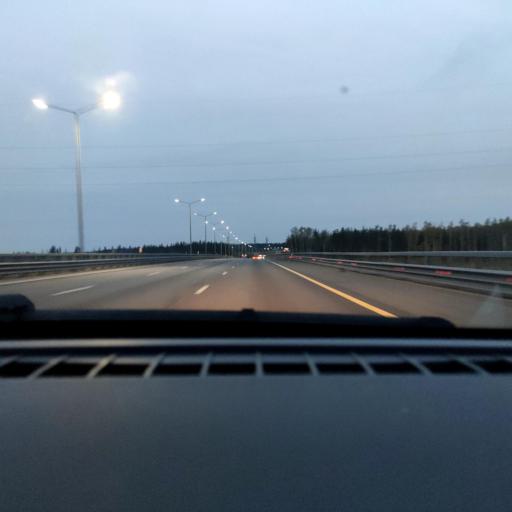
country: RU
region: Voronezj
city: Somovo
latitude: 51.7348
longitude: 39.3097
